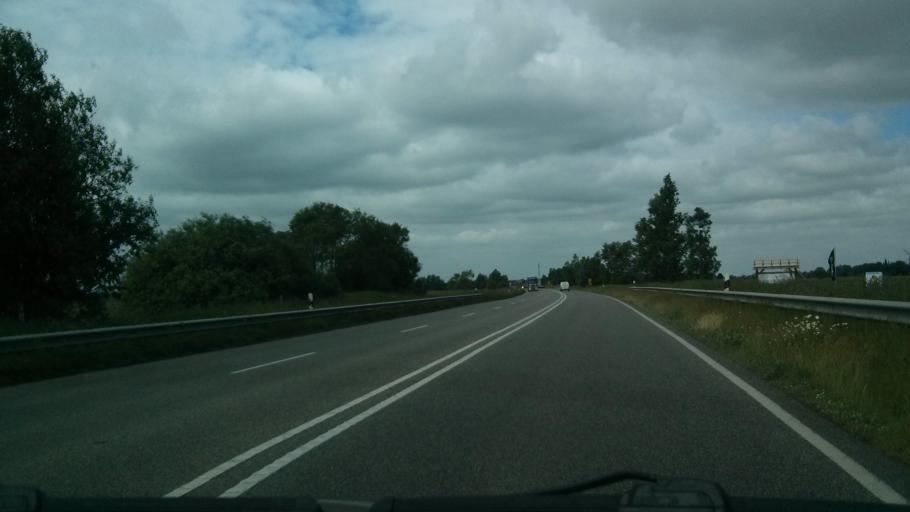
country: DE
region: Lower Saxony
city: Nordenham
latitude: 53.4376
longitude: 8.5296
